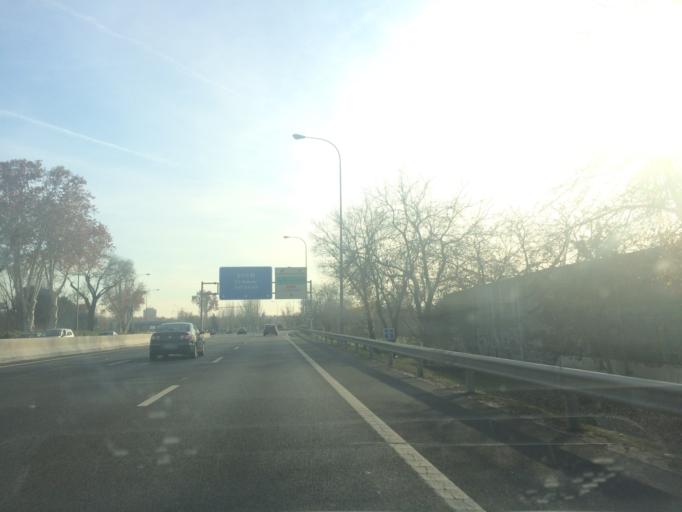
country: ES
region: Madrid
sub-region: Provincia de Madrid
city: Moncloa-Aravaca
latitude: 40.4418
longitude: -3.7391
